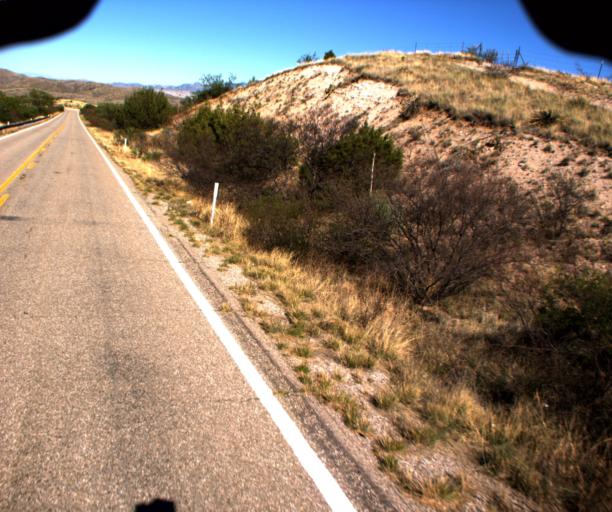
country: US
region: Arizona
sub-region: Pima County
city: Corona de Tucson
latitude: 31.8316
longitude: -110.7071
